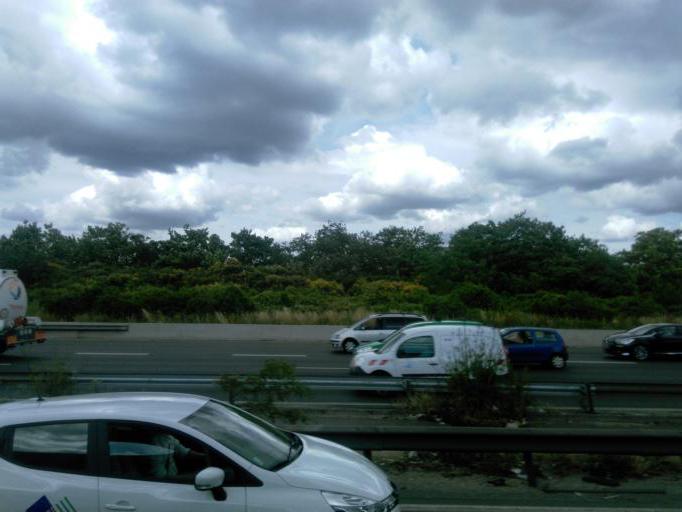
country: FR
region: Ile-de-France
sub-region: Paris
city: Saint-Ouen
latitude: 48.9248
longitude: 2.3406
